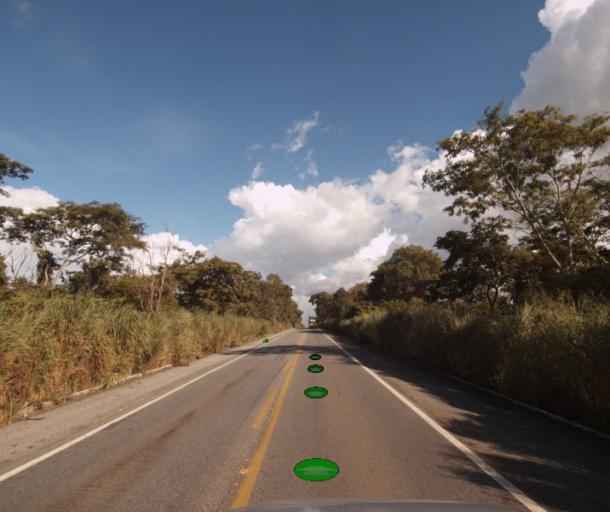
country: BR
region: Goias
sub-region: Porangatu
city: Porangatu
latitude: -13.1627
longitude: -49.1774
